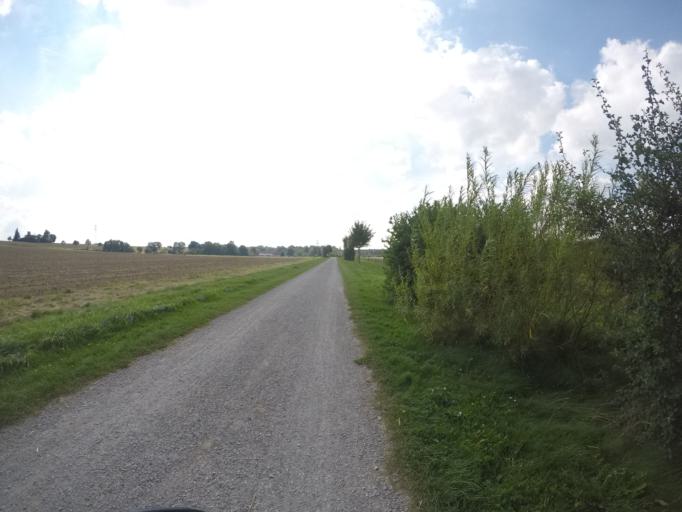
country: DE
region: North Rhine-Westphalia
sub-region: Regierungsbezirk Detmold
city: Bielefeld
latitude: 52.0541
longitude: 8.5828
